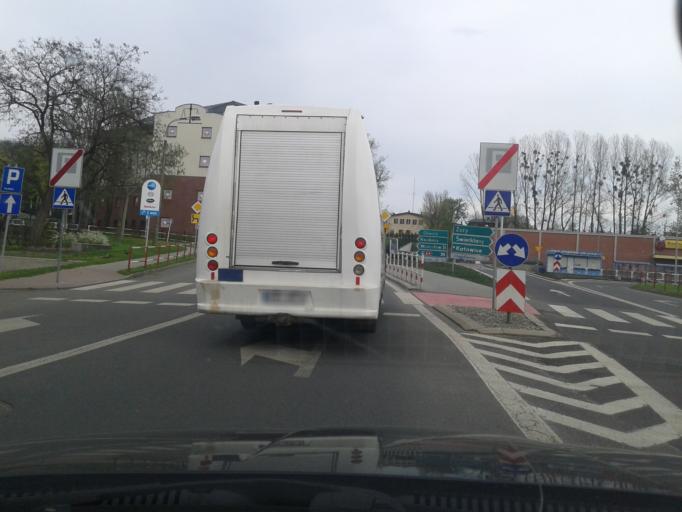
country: PL
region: Silesian Voivodeship
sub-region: Rybnik
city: Rybnik
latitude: 50.0887
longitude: 18.5430
